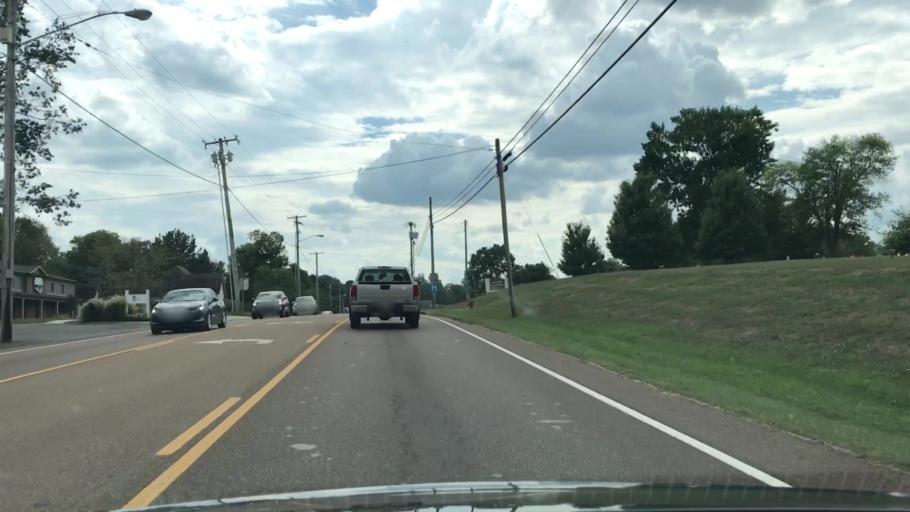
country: US
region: Tennessee
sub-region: Maury County
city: Spring Hill
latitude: 35.7558
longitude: -86.9256
